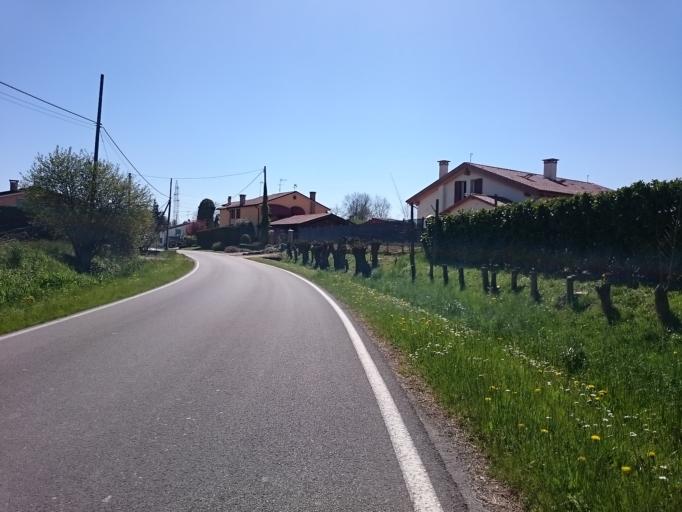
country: IT
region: Veneto
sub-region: Provincia di Padova
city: Legnaro
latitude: 45.3232
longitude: 11.9689
